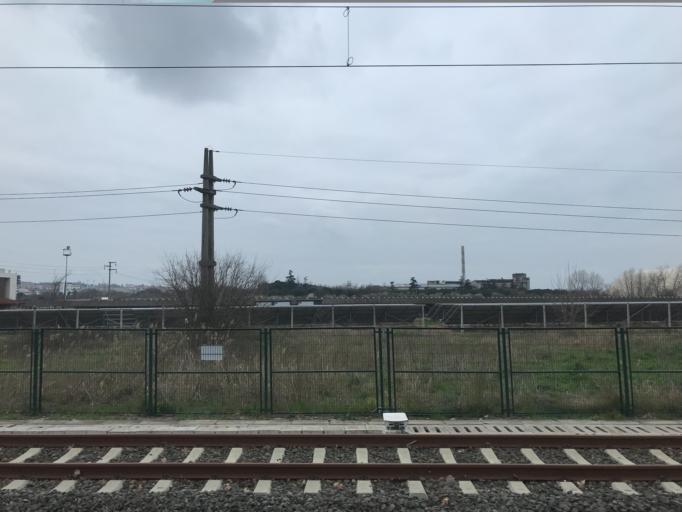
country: TR
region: Kocaeli
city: Darica
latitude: 40.8095
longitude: 29.3536
